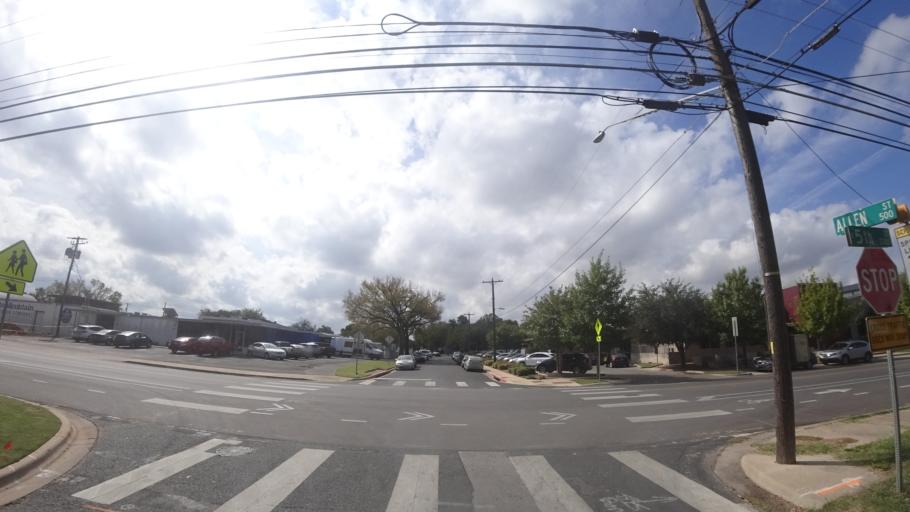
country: US
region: Texas
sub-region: Travis County
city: Austin
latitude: 30.2549
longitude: -97.7056
